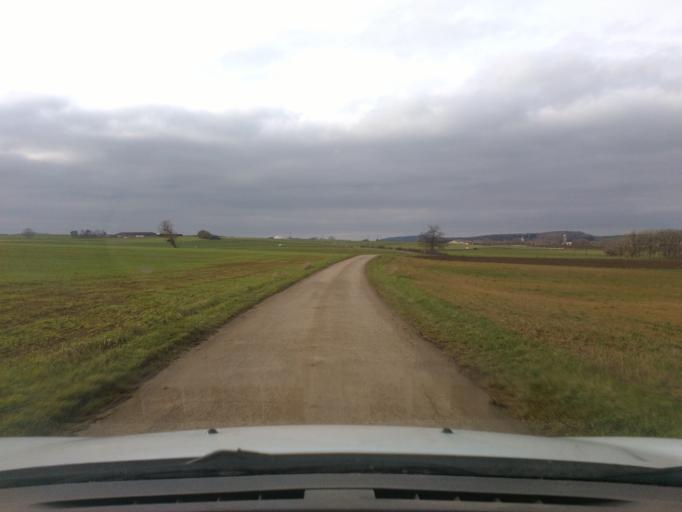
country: FR
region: Lorraine
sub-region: Departement des Vosges
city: Mirecourt
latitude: 48.3287
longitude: 6.0401
